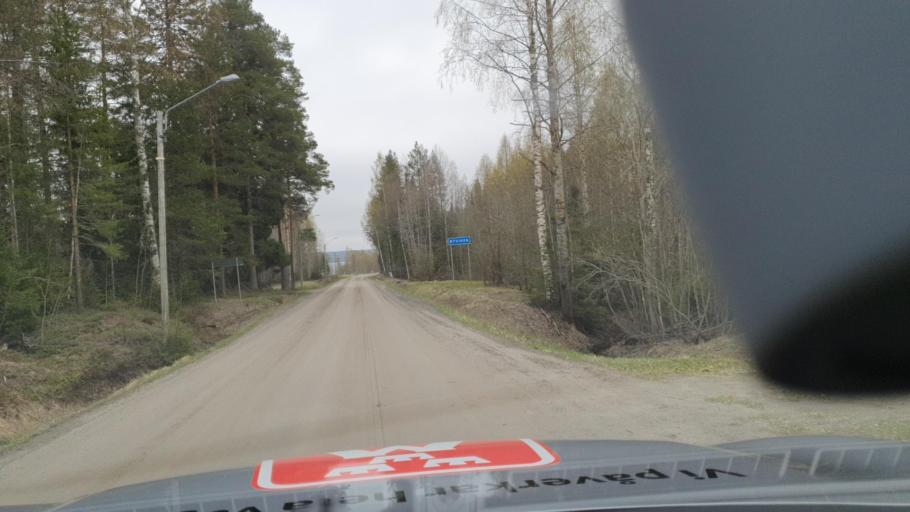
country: SE
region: Vaesterbotten
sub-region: Bjurholms Kommun
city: Bjurholm
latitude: 63.6486
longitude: 19.0498
